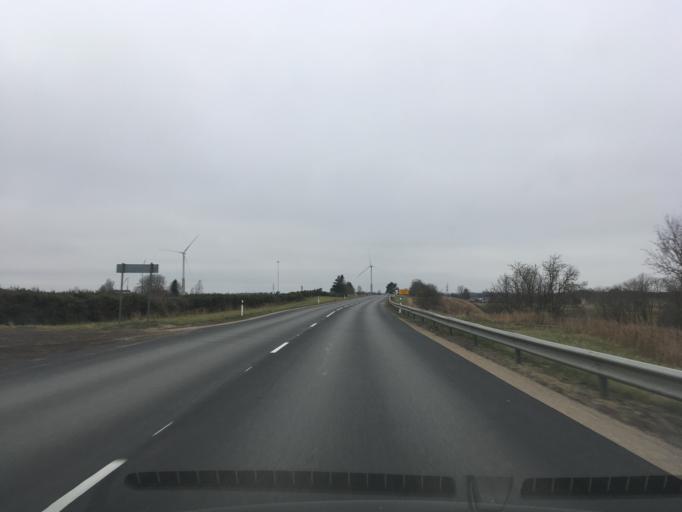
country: EE
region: Ida-Virumaa
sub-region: Aseri vald
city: Aseri
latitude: 59.4432
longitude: 26.7877
